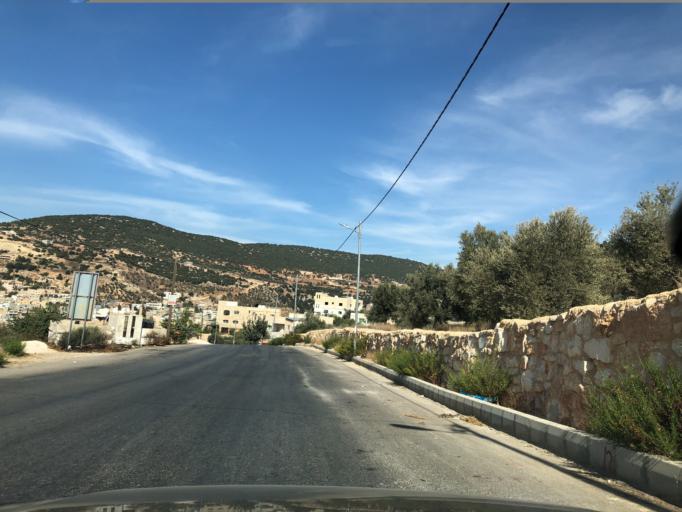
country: JO
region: Irbid
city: `Ayn Jannah
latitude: 32.3285
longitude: 35.7602
